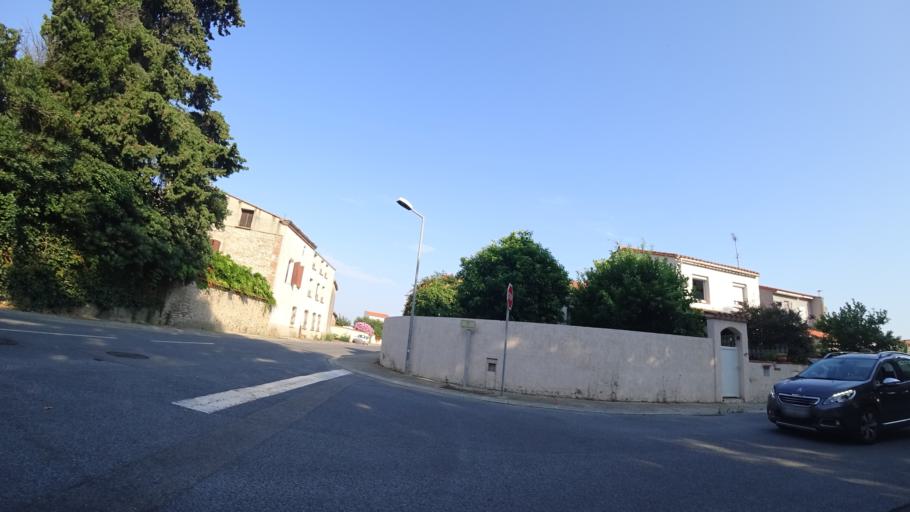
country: FR
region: Languedoc-Roussillon
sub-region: Departement des Pyrenees-Orientales
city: Sainte-Marie-Plage
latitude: 42.7288
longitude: 3.0152
